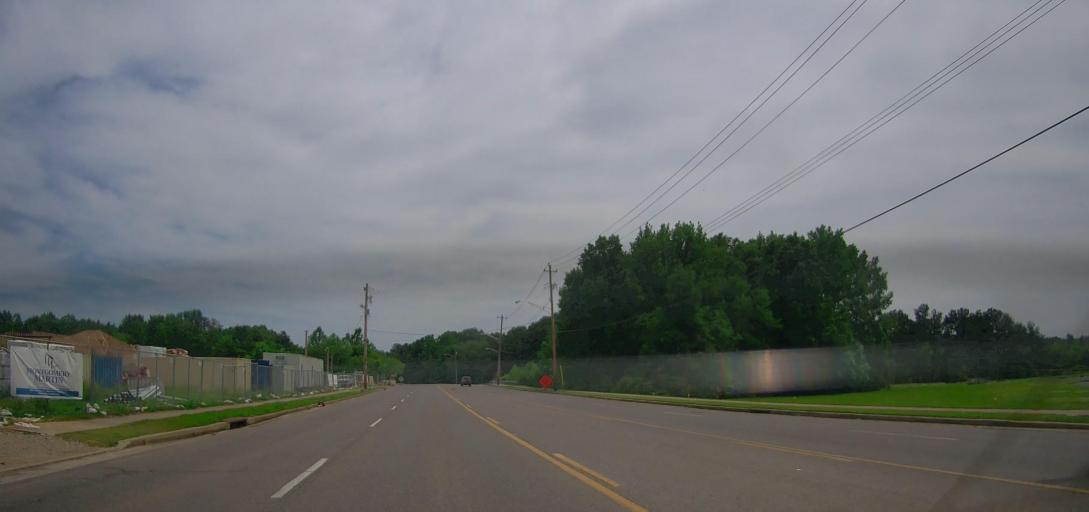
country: US
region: Tennessee
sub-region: Shelby County
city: Germantown
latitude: 35.0744
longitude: -89.8498
